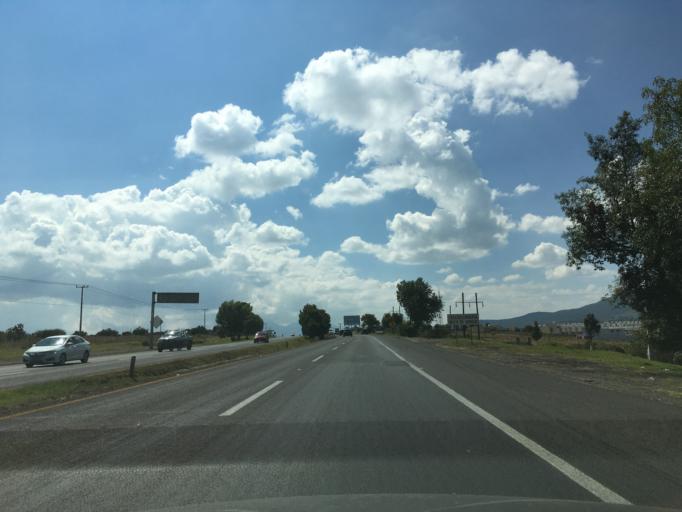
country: MX
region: Michoacan
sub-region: Morelia
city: La Mintzita (Piedra Dura)
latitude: 19.6300
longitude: -101.2746
